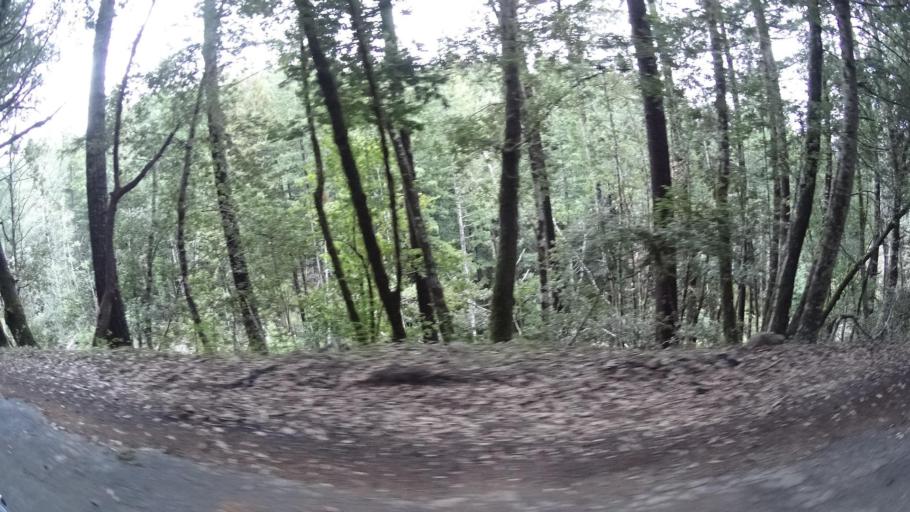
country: US
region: California
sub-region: Humboldt County
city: Blue Lake
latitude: 40.8619
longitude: -123.9103
